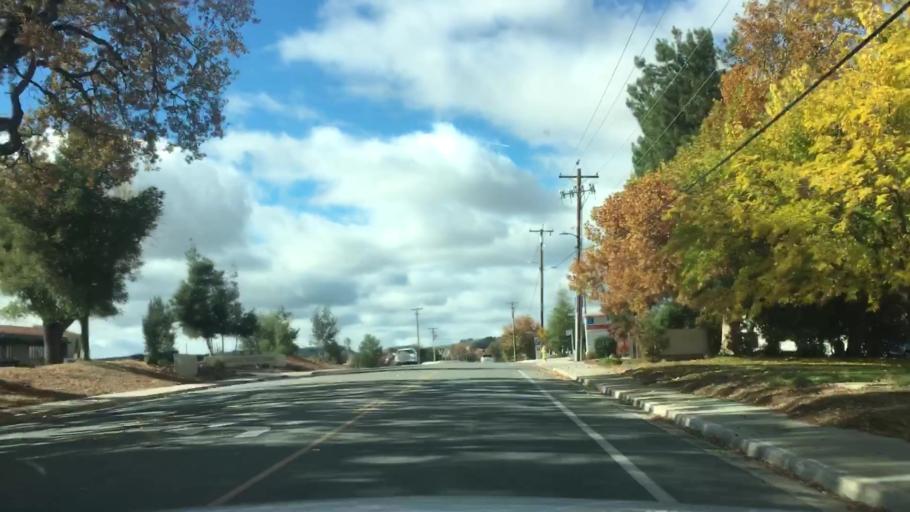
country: US
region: California
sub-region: San Luis Obispo County
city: Templeton
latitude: 35.5544
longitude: -120.7183
